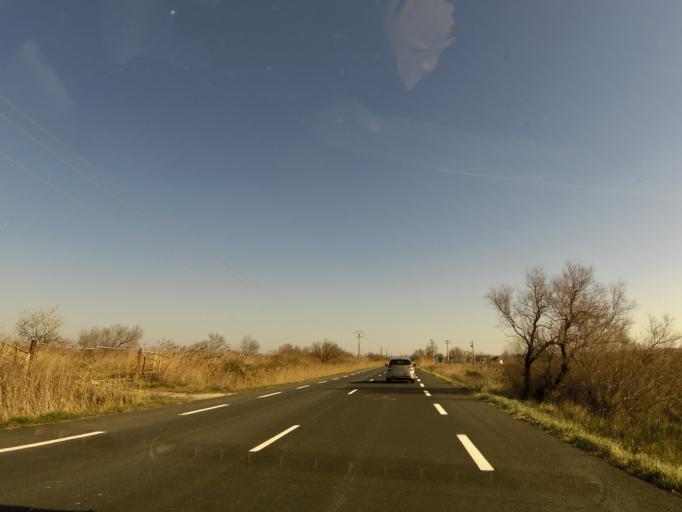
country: FR
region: Languedoc-Roussillon
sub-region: Departement du Gard
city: Aigues-Mortes
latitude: 43.5535
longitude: 4.3282
